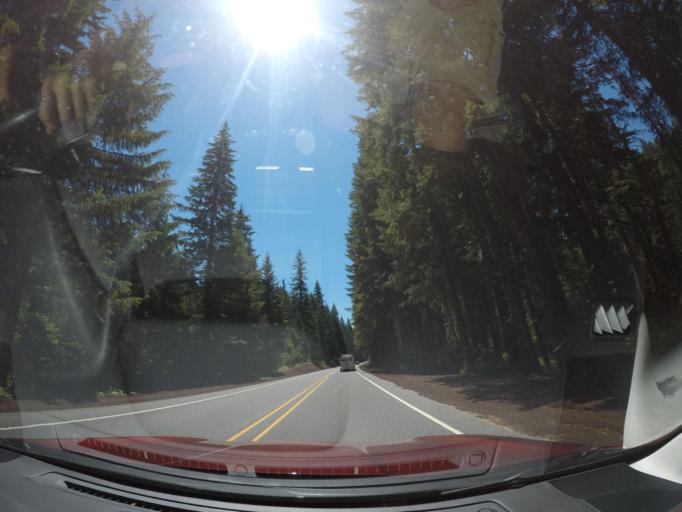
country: US
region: Oregon
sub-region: Deschutes County
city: Sisters
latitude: 44.5397
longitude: -121.9954
